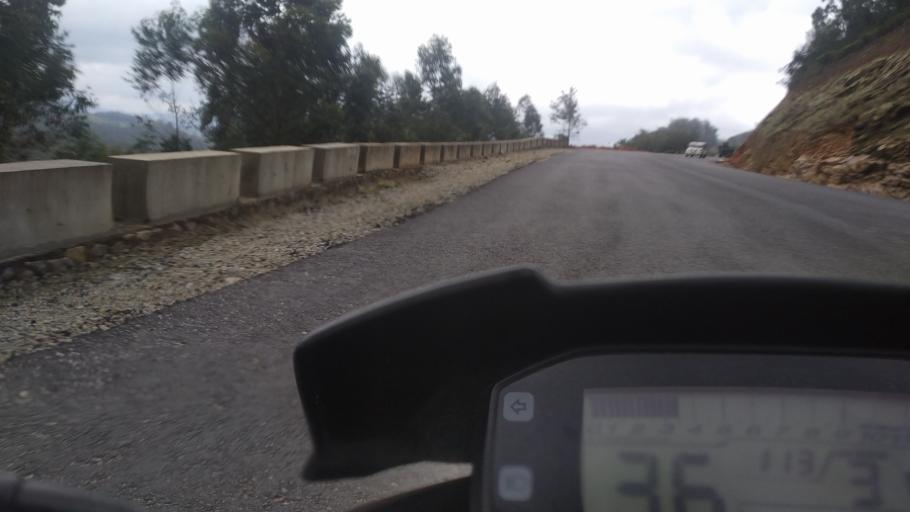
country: IN
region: Kerala
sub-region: Idukki
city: Munnar
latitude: 10.0808
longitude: 77.0799
